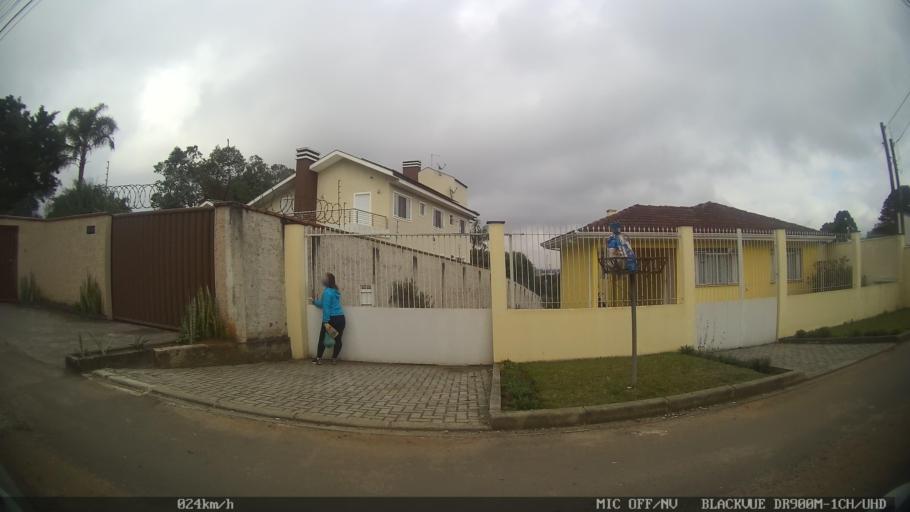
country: BR
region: Parana
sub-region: Curitiba
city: Curitiba
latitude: -25.3661
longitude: -49.2398
